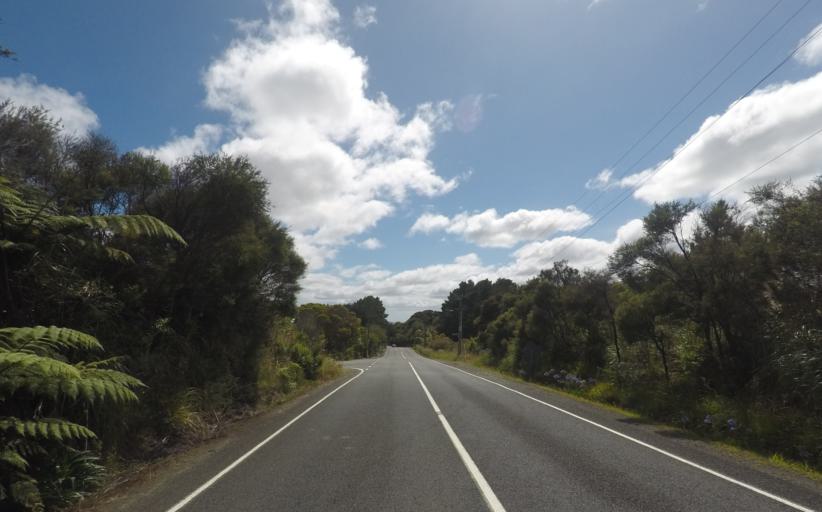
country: NZ
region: Auckland
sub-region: Auckland
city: Muriwai Beach
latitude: -36.8580
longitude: 174.5229
